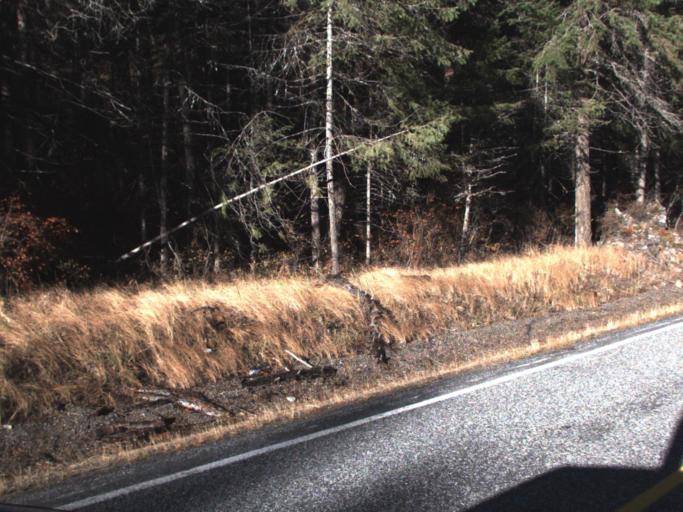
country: US
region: Washington
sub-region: Ferry County
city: Republic
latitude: 48.3641
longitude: -118.7432
